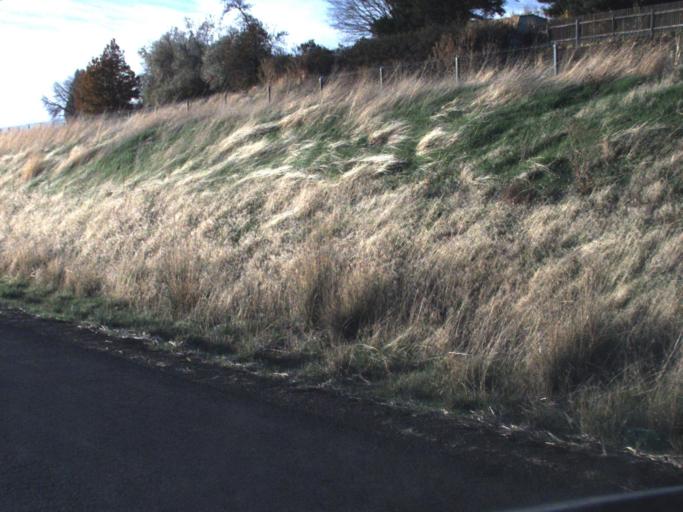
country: US
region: Washington
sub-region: Walla Walla County
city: Walla Walla East
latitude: 46.0813
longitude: -118.3021
